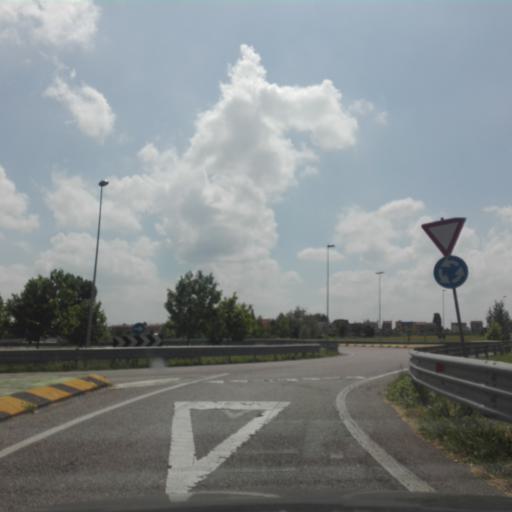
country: IT
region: Veneto
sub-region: Provincia di Rovigo
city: Villadose
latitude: 45.0726
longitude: 11.8772
